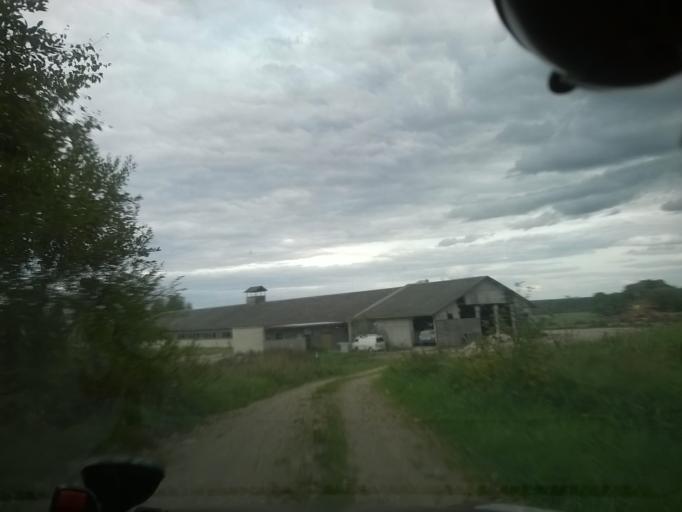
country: EE
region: Vorumaa
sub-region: Voru linn
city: Voru
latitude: 57.8075
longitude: 27.1659
